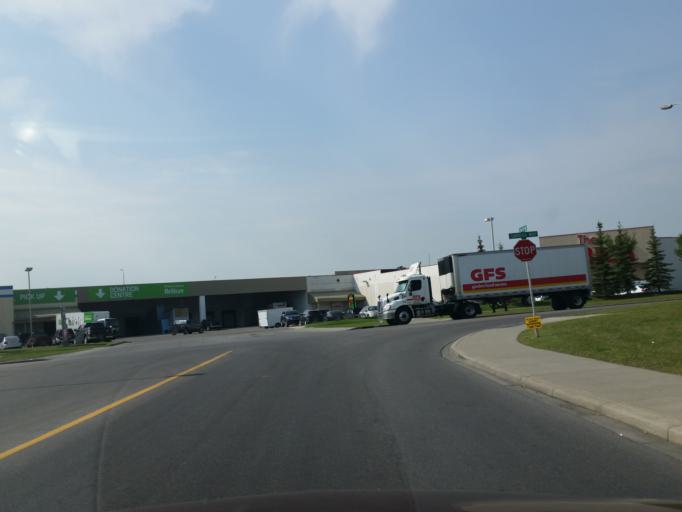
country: CA
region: Alberta
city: Calgary
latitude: 51.0691
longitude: -113.9860
